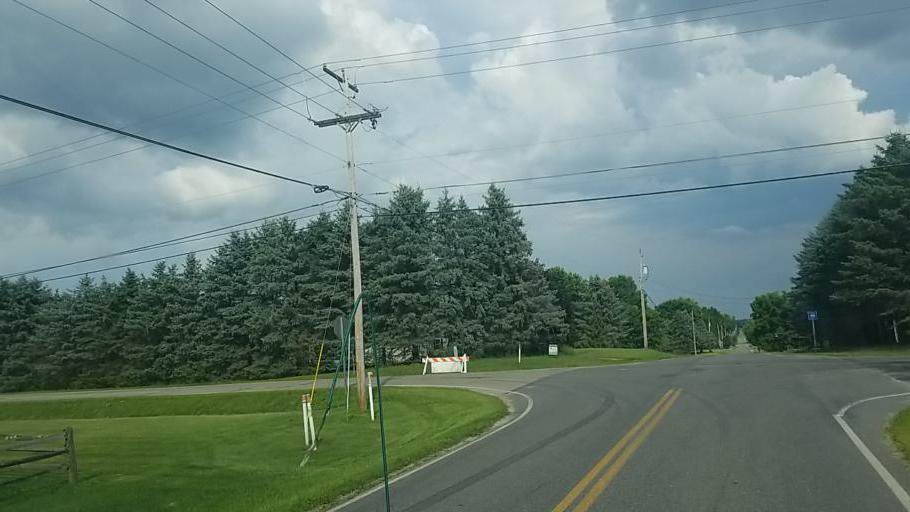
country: US
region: Ohio
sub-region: Medina County
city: Westfield Center
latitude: 41.0120
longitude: -81.9112
